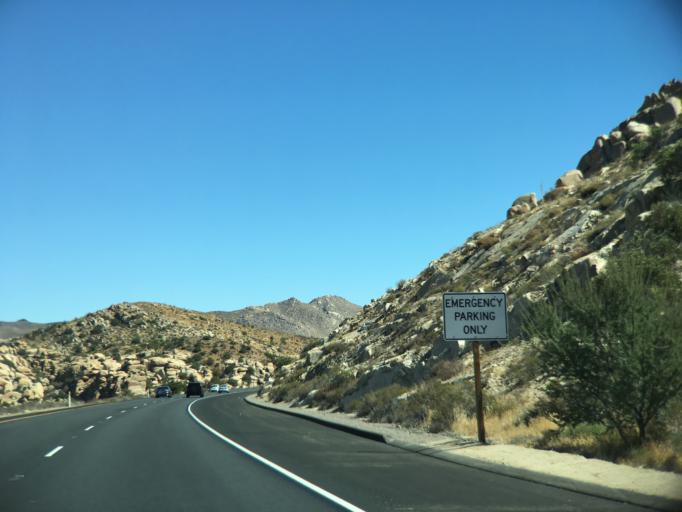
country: MX
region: Baja California
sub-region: Tecate
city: Cereso del Hongo
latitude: 32.6609
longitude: -116.2109
